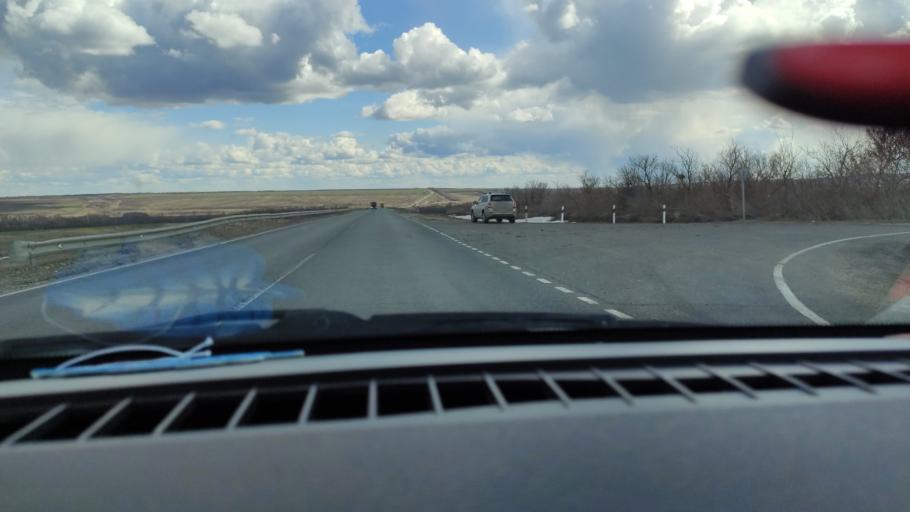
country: RU
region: Saratov
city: Dukhovnitskoye
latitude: 52.7543
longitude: 48.2459
